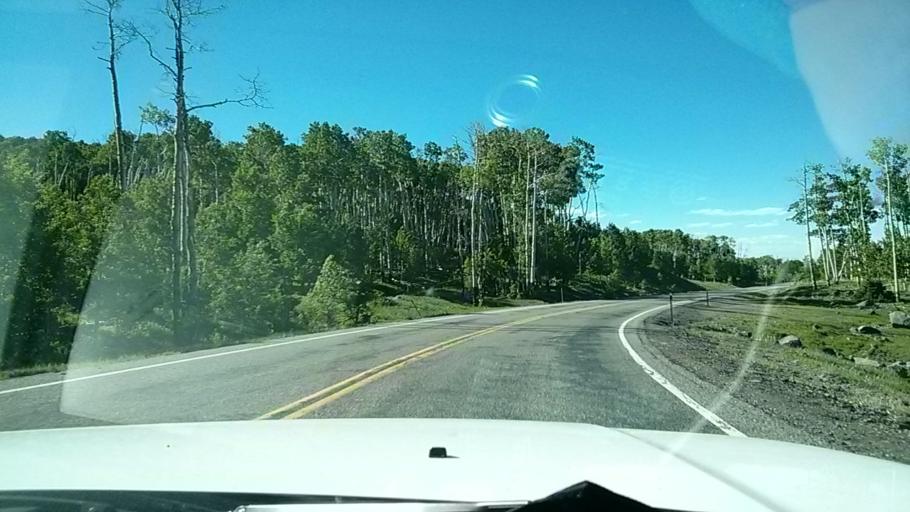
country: US
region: Utah
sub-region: Wayne County
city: Loa
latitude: 38.0588
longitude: -111.3282
